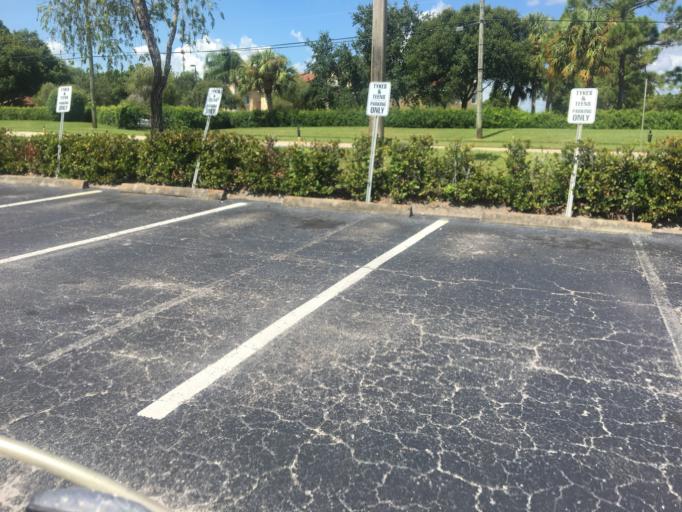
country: US
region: Florida
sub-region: Martin County
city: Palm City
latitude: 27.1683
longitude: -80.3020
